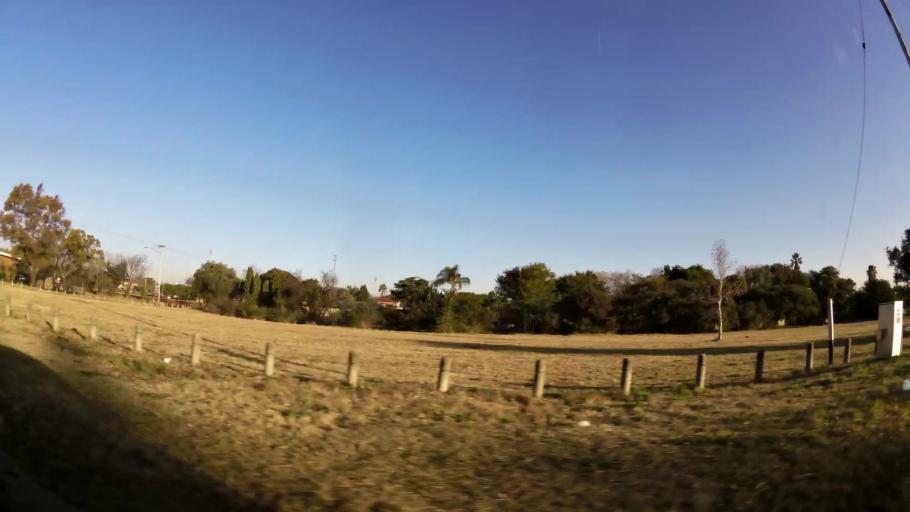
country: ZA
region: Gauteng
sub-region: City of Tshwane Metropolitan Municipality
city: Pretoria
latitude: -25.7011
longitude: 28.2371
